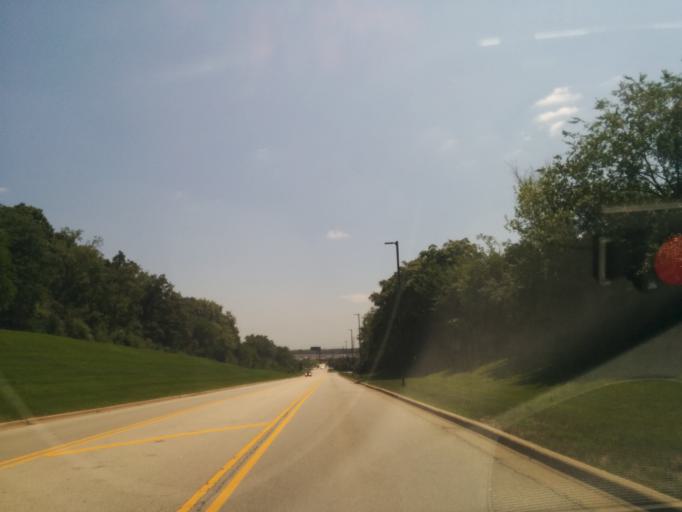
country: US
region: Illinois
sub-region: Cook County
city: Indian Head Park
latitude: 41.7534
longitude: -87.8847
